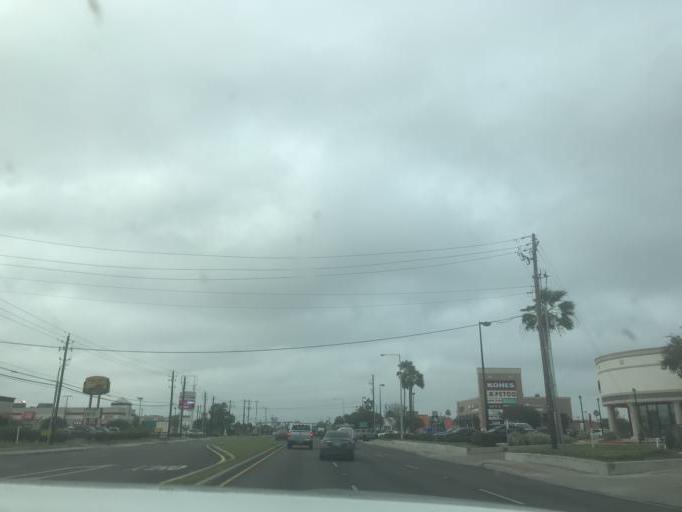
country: US
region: Texas
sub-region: Nueces County
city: Corpus Christi
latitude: 27.6841
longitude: -97.3810
